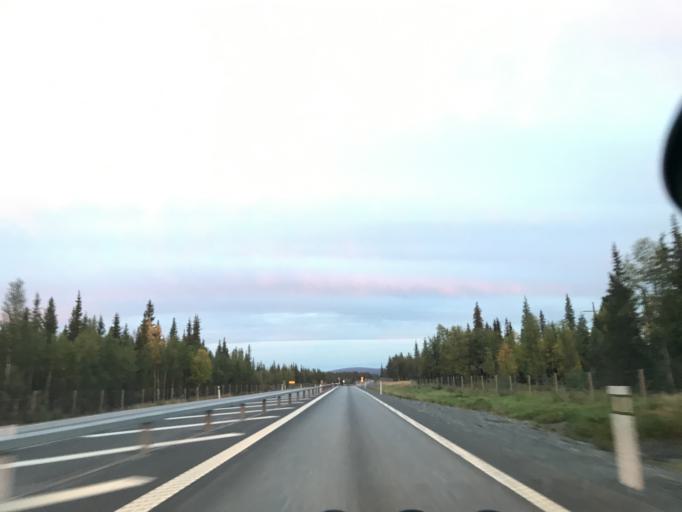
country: SE
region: Norrbotten
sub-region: Gallivare Kommun
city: Malmberget
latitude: 67.6888
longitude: 20.8425
